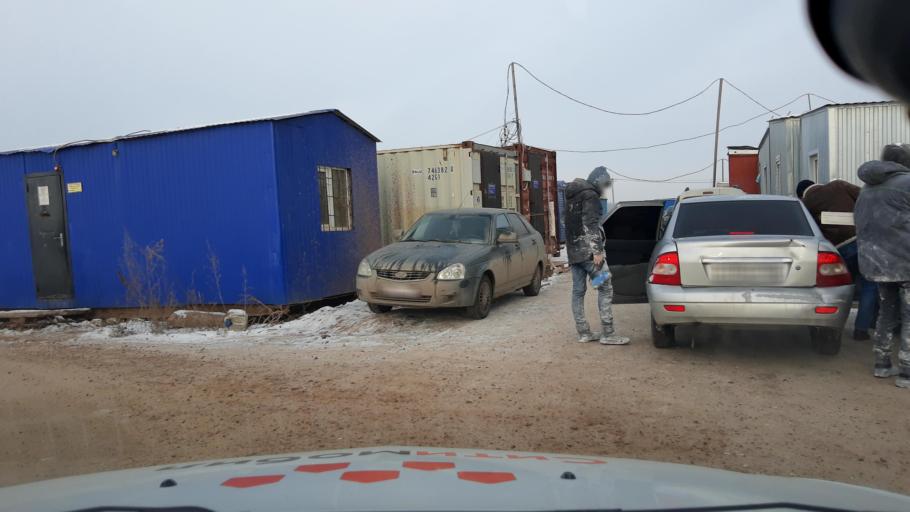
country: RU
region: Bashkortostan
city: Ufa
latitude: 54.7794
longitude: 55.9599
